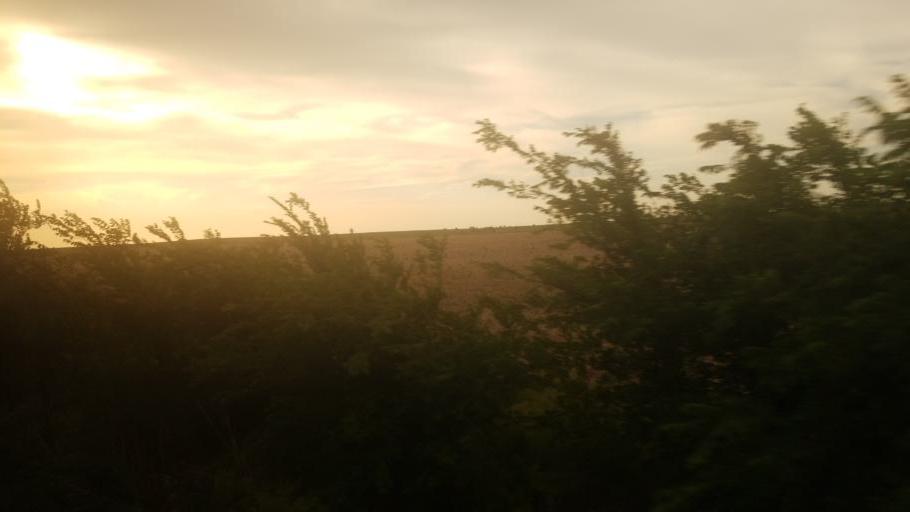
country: US
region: Kansas
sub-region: Lyon County
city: Emporia
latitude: 38.4435
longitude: -96.1054
